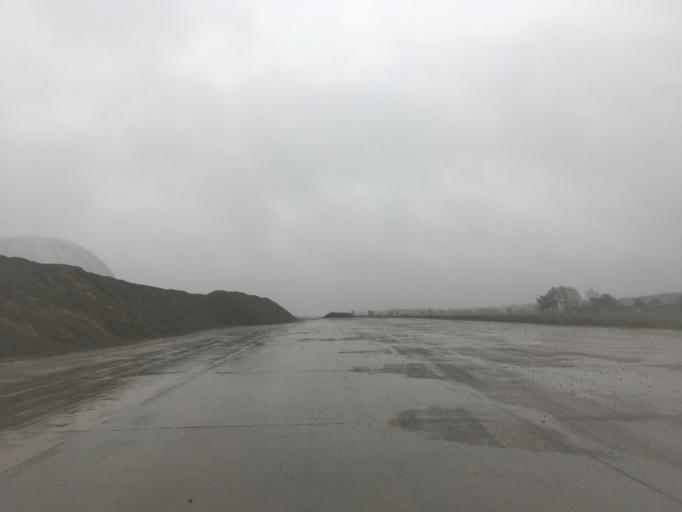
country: DE
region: Brandenburg
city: Halbe
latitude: 52.0364
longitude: 13.7366
